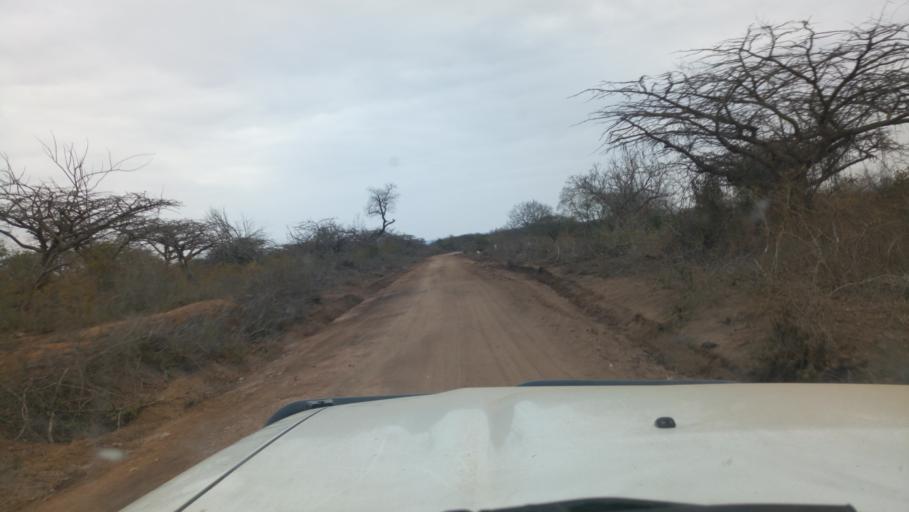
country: KE
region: Makueni
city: Wote
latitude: -1.8896
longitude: 38.1395
